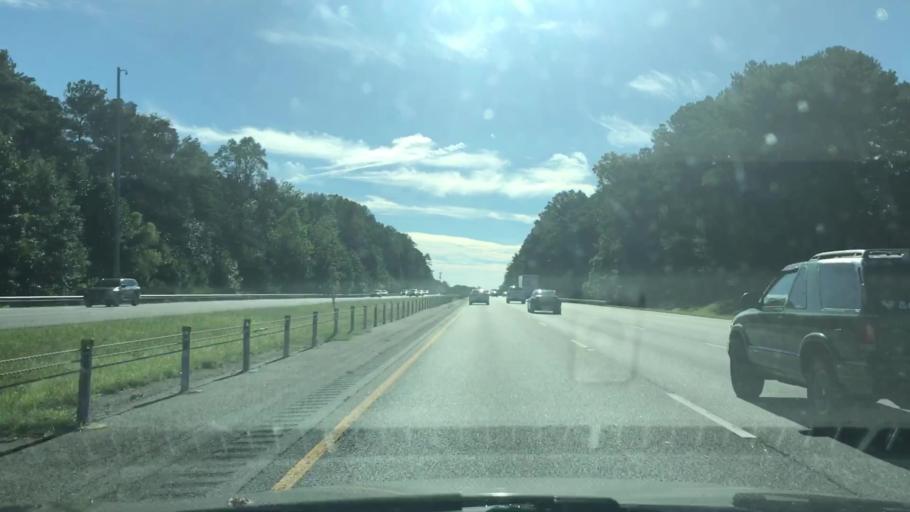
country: US
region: Georgia
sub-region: DeKalb County
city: Tucker
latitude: 33.8344
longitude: -84.1943
